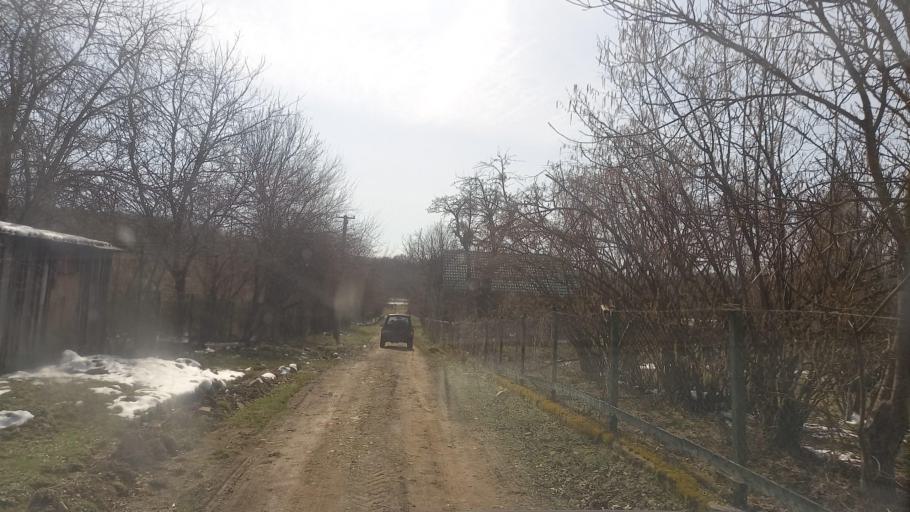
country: RU
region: Krasnodarskiy
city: Smolenskaya
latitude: 44.6032
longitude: 38.8525
